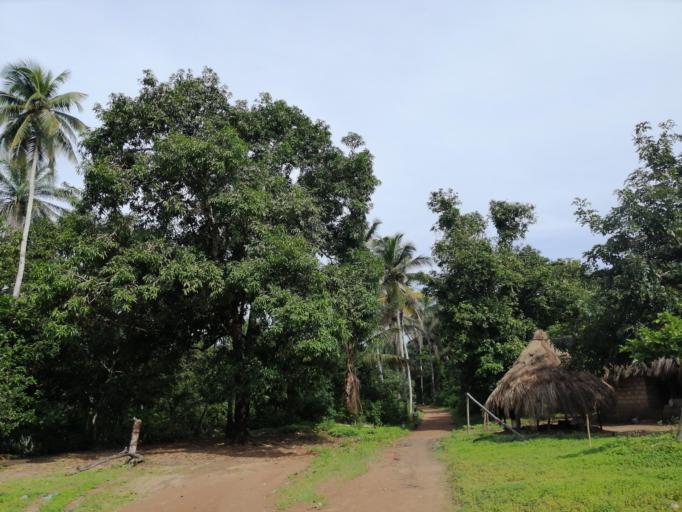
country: SL
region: Northern Province
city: Port Loko
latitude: 8.7896
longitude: -12.9291
